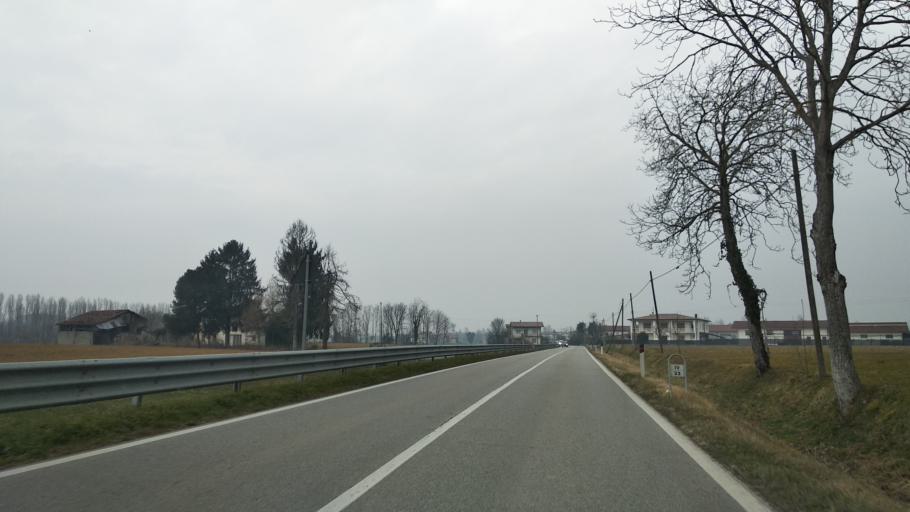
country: IT
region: Veneto
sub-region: Provincia di Padova
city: Villa del Conte
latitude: 45.5655
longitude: 11.8659
